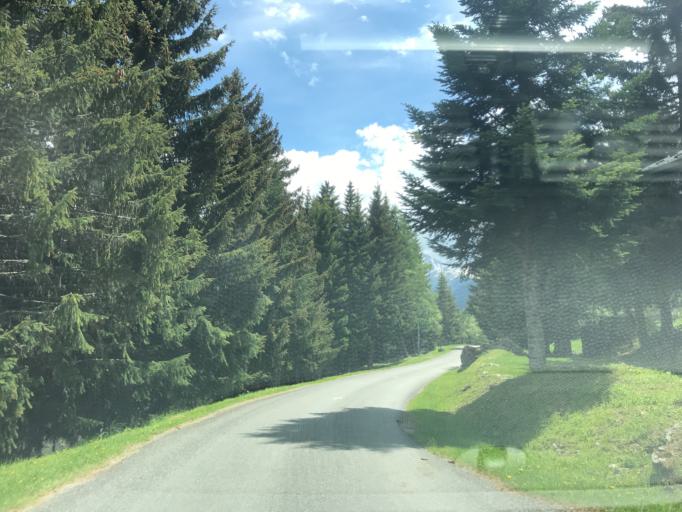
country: FR
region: Rhone-Alpes
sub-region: Departement de la Savoie
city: Modane
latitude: 45.2194
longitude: 6.6494
